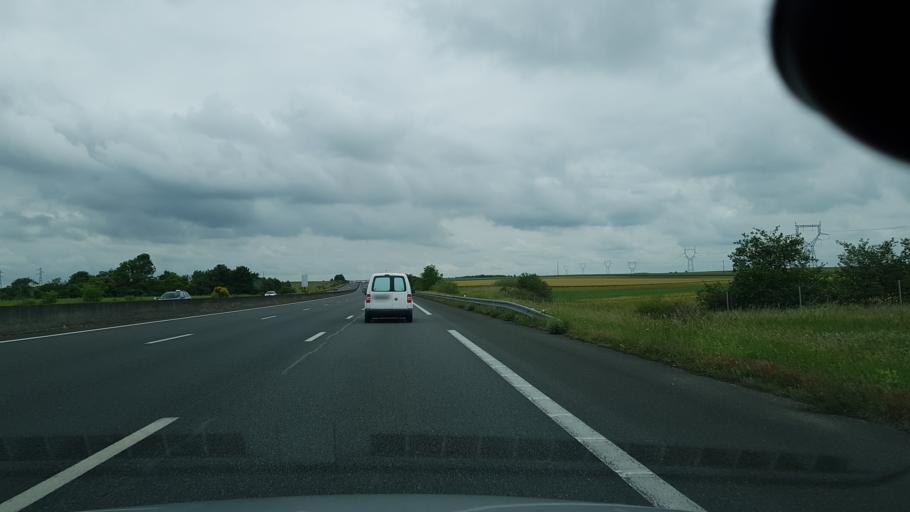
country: FR
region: Centre
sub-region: Departement du Loir-et-Cher
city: Suevres
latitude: 47.7039
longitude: 1.4505
